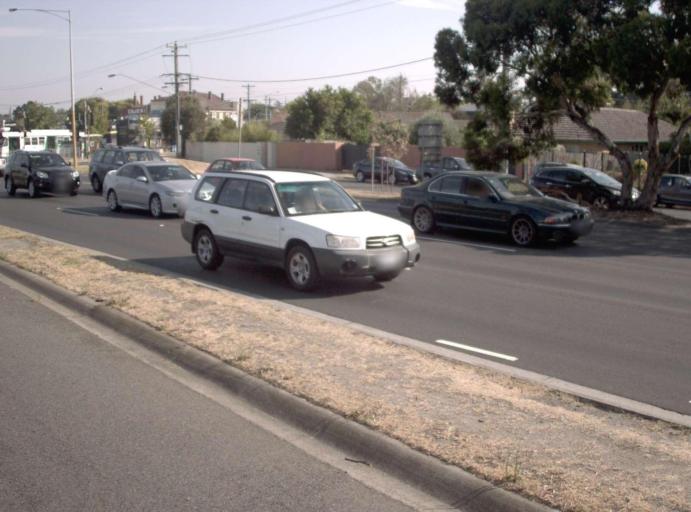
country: AU
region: Victoria
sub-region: Bayside
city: Brighton East
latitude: -37.9152
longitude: 145.0172
